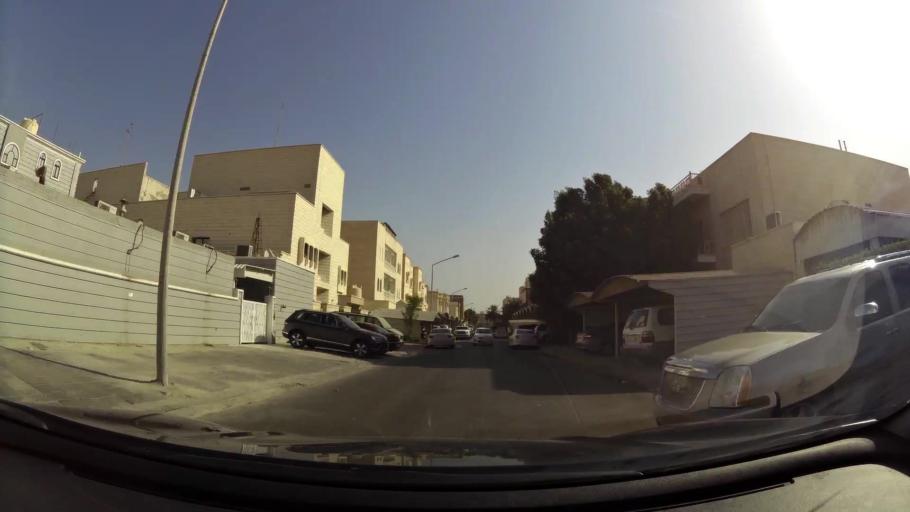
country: KW
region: Muhafazat Hawalli
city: Salwa
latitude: 29.2924
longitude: 48.0768
